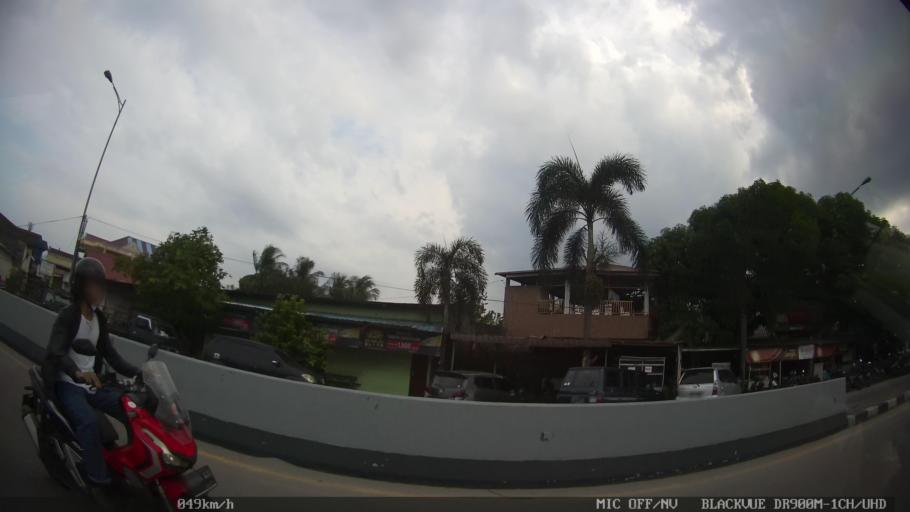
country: ID
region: North Sumatra
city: Medan
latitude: 3.5405
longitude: 98.6520
